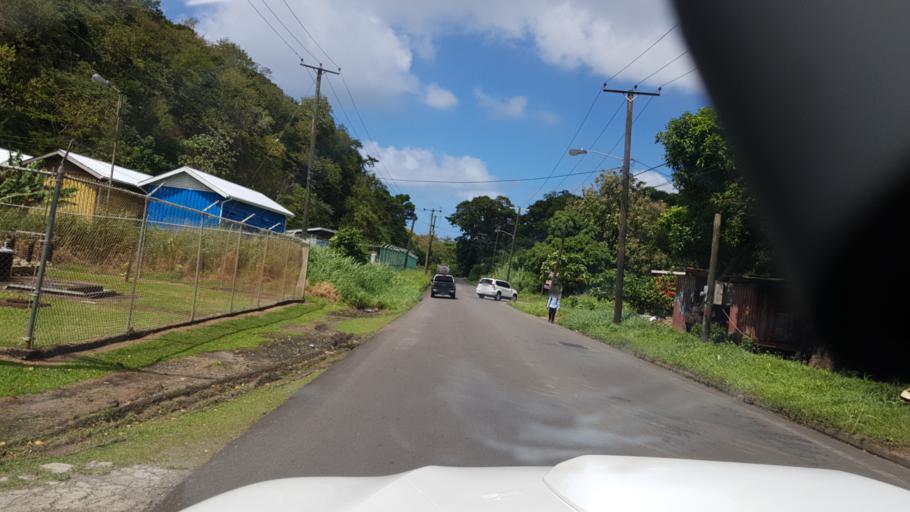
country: LC
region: Castries Quarter
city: Bisee
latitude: 14.0285
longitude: -60.9638
